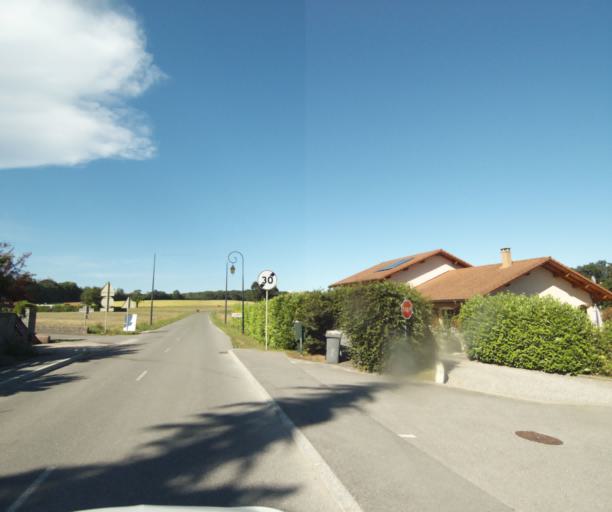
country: FR
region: Rhone-Alpes
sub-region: Departement de la Haute-Savoie
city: Massongy
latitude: 46.3510
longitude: 6.3334
